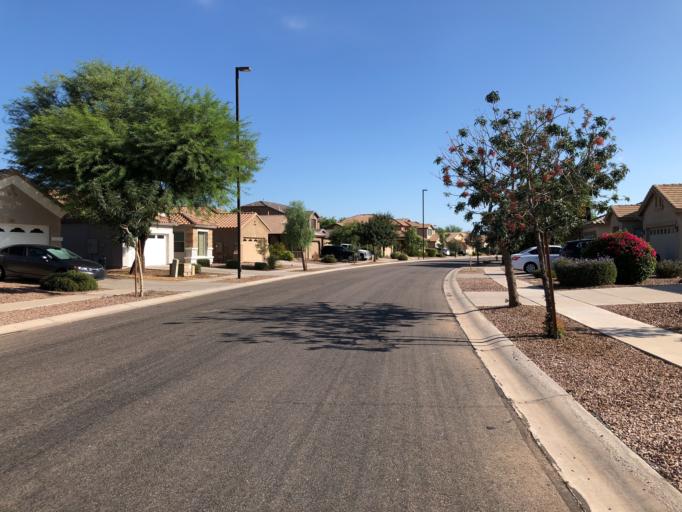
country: US
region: Arizona
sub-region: Maricopa County
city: Queen Creek
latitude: 33.2797
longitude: -111.7041
